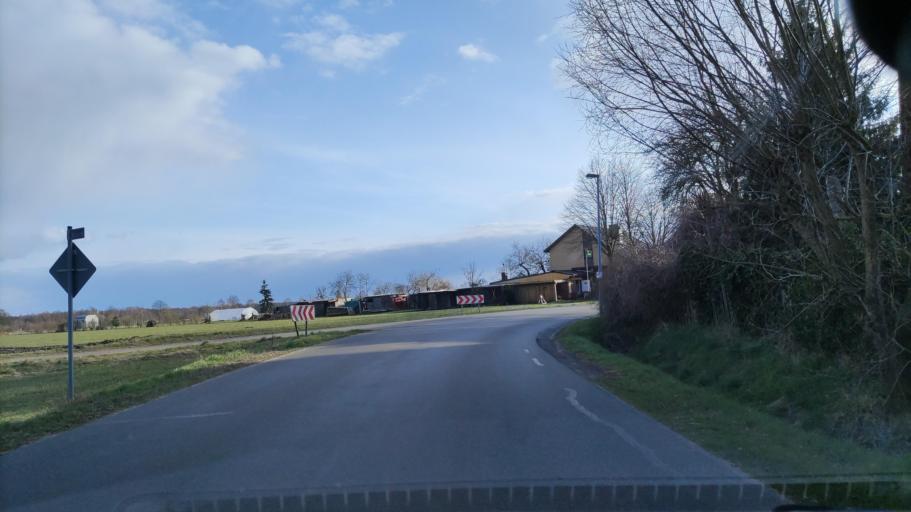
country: DE
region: Lower Saxony
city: Klein Gusborn
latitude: 53.0559
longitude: 11.2299
